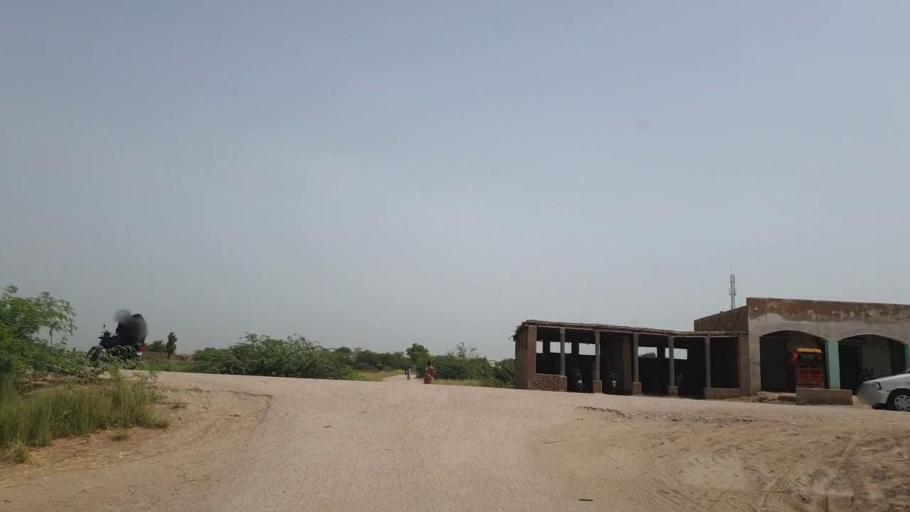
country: PK
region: Sindh
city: Sakrand
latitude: 26.1412
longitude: 68.3642
